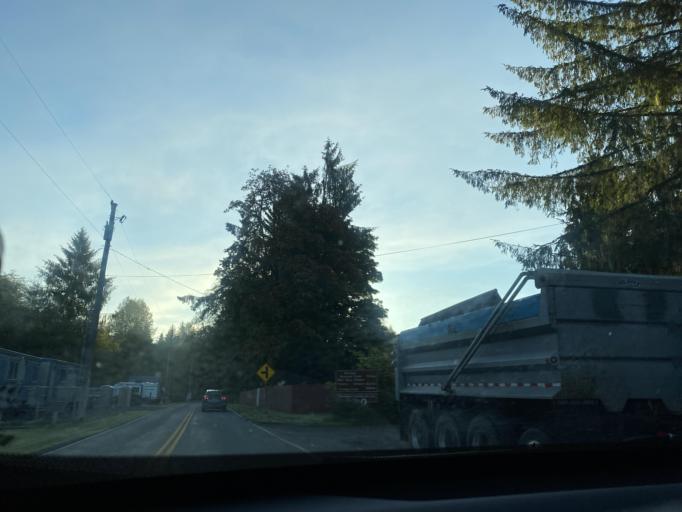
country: US
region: Washington
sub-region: Clallam County
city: Forks
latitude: 47.8167
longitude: -124.1561
